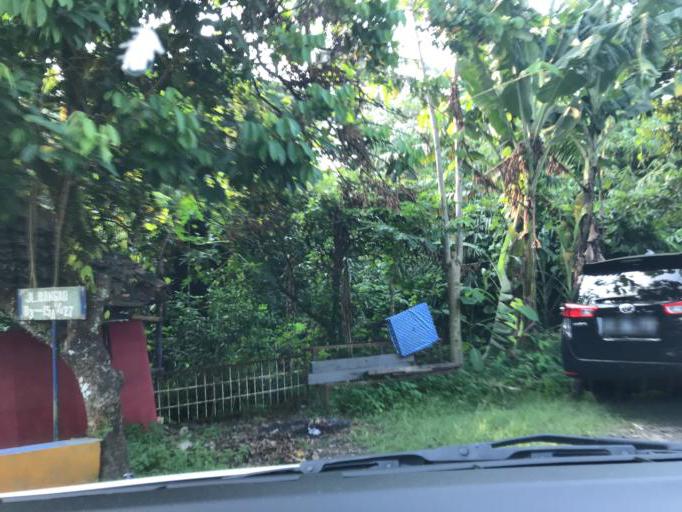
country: ID
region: West Java
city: Cibinong
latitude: -6.4729
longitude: 106.8182
